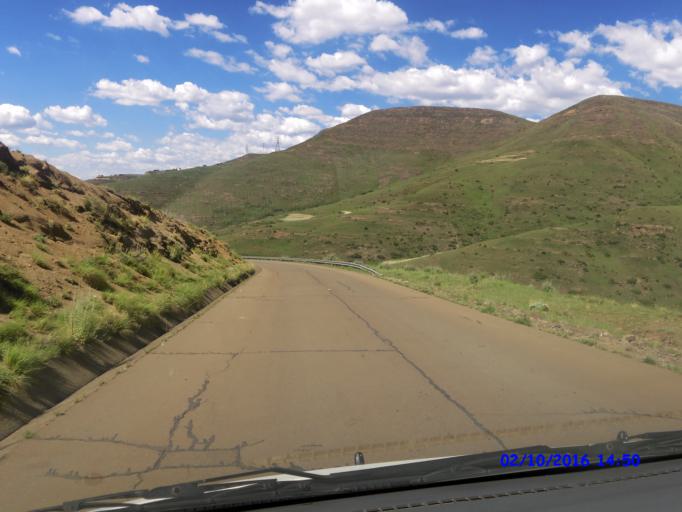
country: LS
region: Maseru
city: Nako
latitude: -29.4910
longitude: 28.0626
